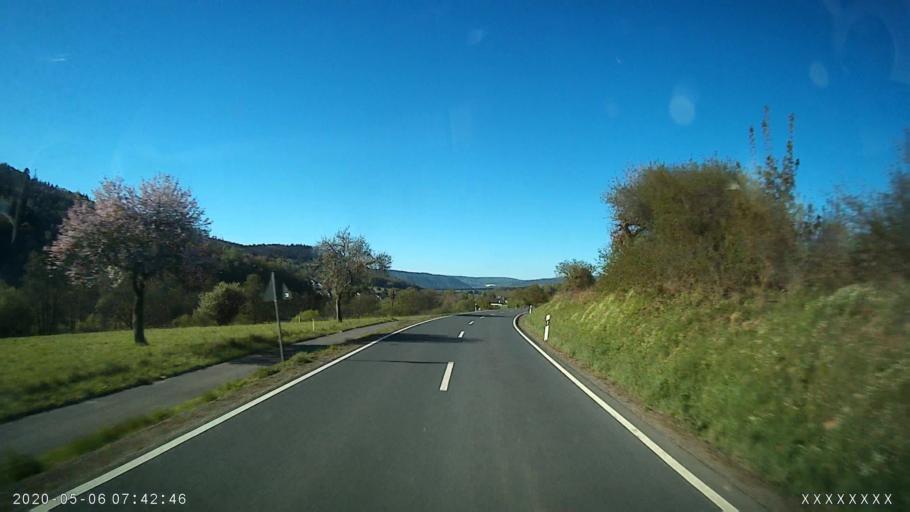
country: DE
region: Hesse
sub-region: Regierungsbezirk Giessen
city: Haiger
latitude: 50.7781
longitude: 8.2143
